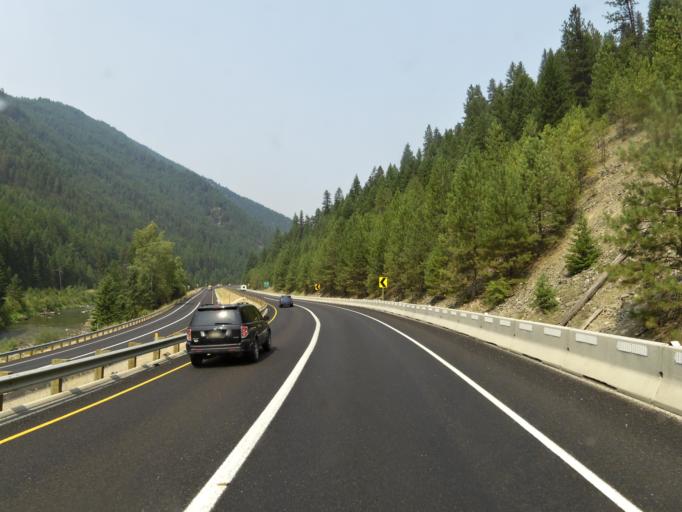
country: US
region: Montana
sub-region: Sanders County
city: Thompson Falls
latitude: 47.3144
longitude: -115.2361
